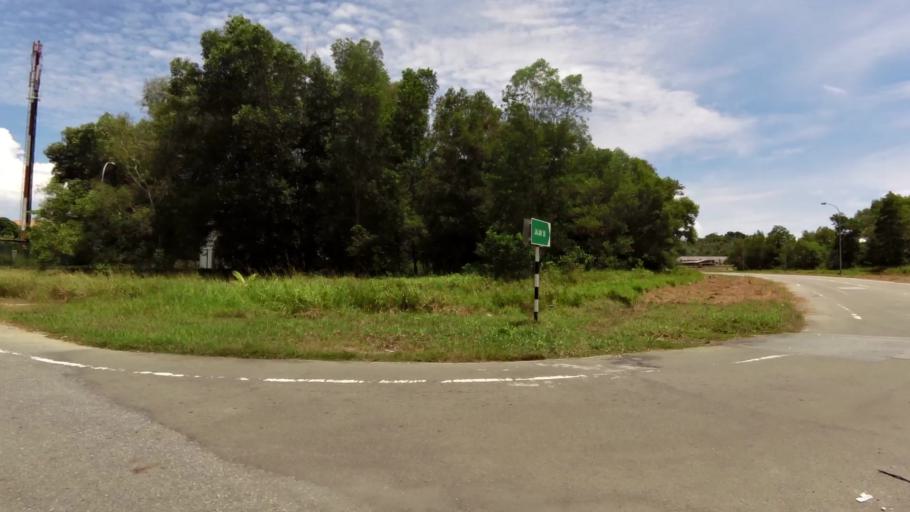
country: BN
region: Brunei and Muara
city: Bandar Seri Begawan
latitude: 4.9646
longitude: 114.9126
